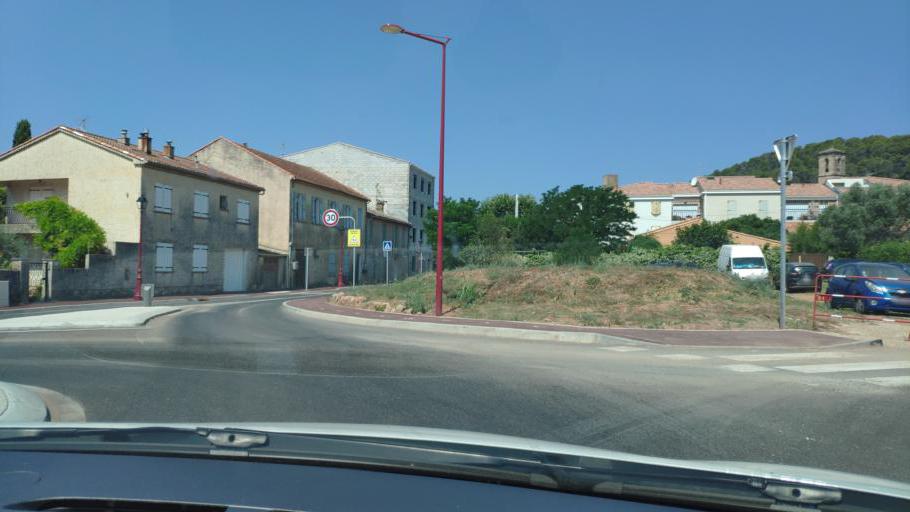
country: FR
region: Provence-Alpes-Cote d'Azur
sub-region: Departement du Var
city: Les Arcs
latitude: 43.4630
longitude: 6.4828
